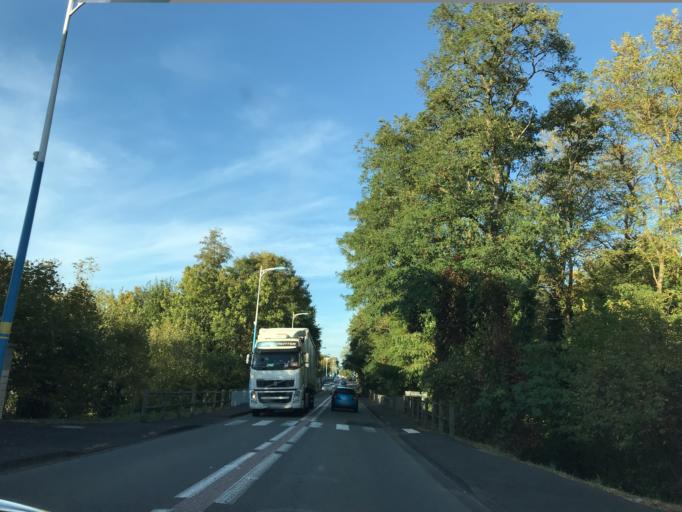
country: FR
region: Auvergne
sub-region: Departement du Puy-de-Dome
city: Puy-Guillaume
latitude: 45.9621
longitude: 3.4750
